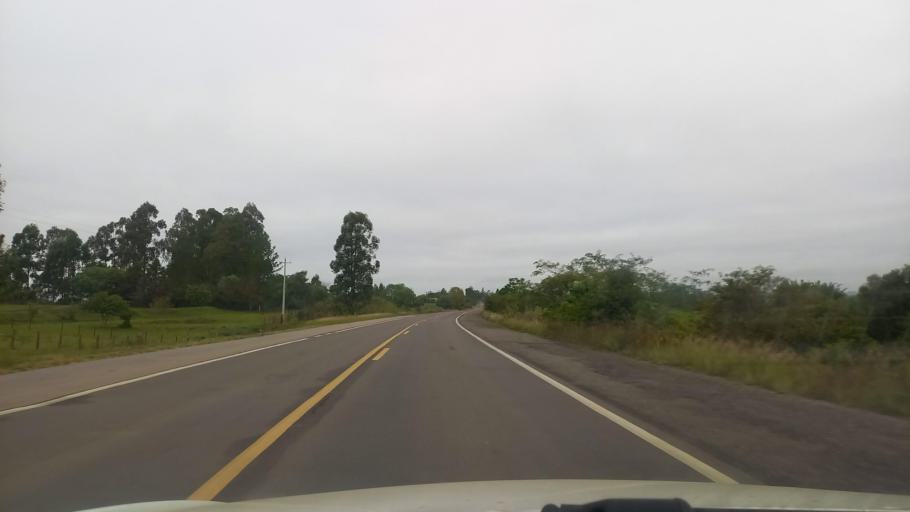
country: BR
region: Rio Grande do Sul
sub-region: Sao Pedro Do Sul
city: Sao Pedro do Sul
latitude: -29.7999
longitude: -54.1215
